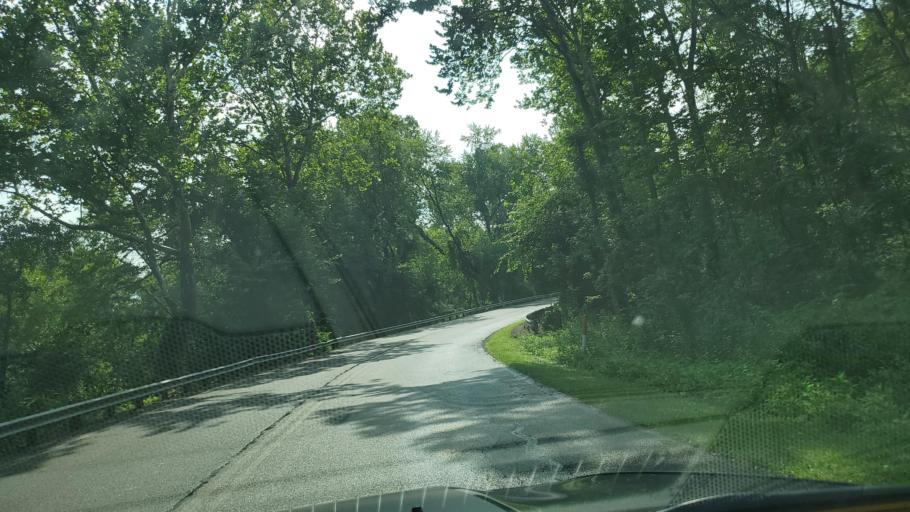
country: US
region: Ohio
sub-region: Mahoning County
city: Lowellville
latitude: 41.0406
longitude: -80.5470
